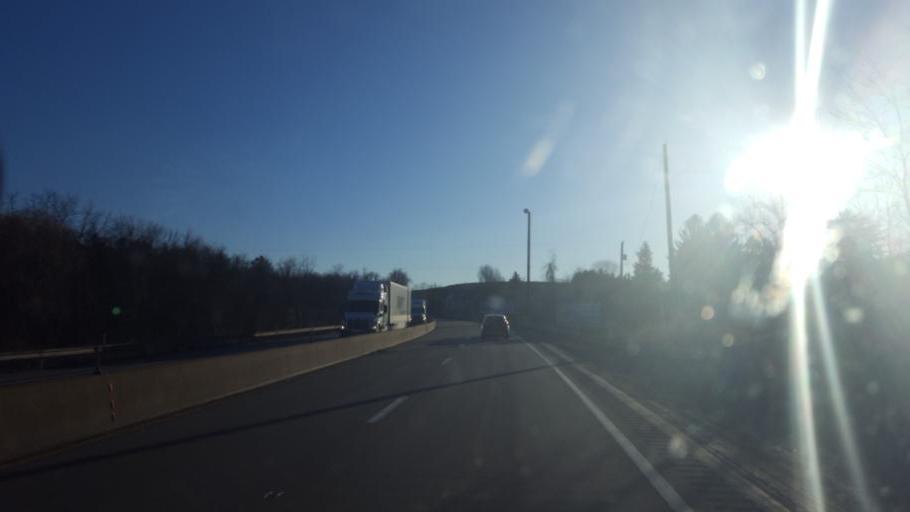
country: US
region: Pennsylvania
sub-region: Westmoreland County
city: West Newton
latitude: 40.1870
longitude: -79.7060
